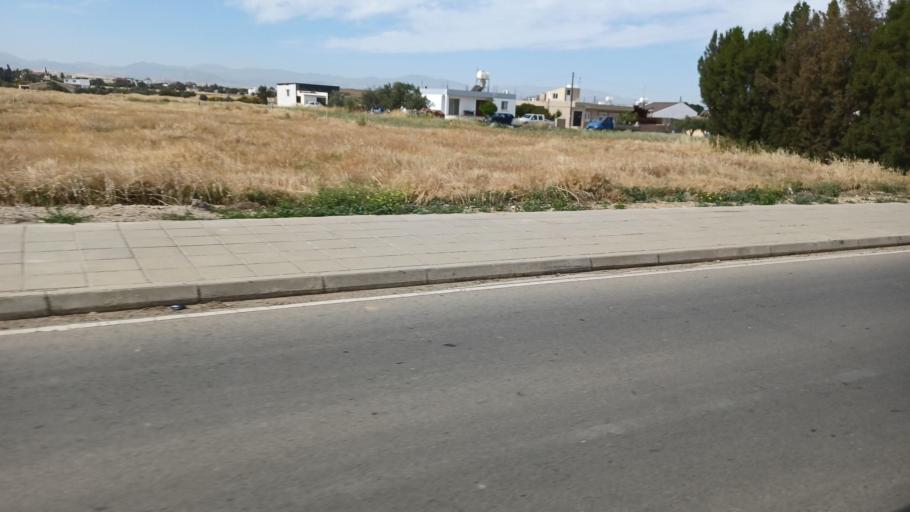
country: CY
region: Lefkosia
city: Kokkinotrimithia
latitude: 35.1554
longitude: 33.1902
